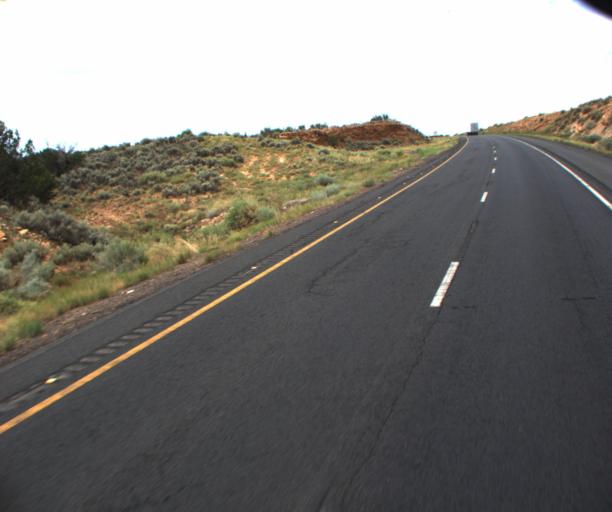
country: US
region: Arizona
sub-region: Apache County
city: Houck
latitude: 35.2756
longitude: -109.2614
